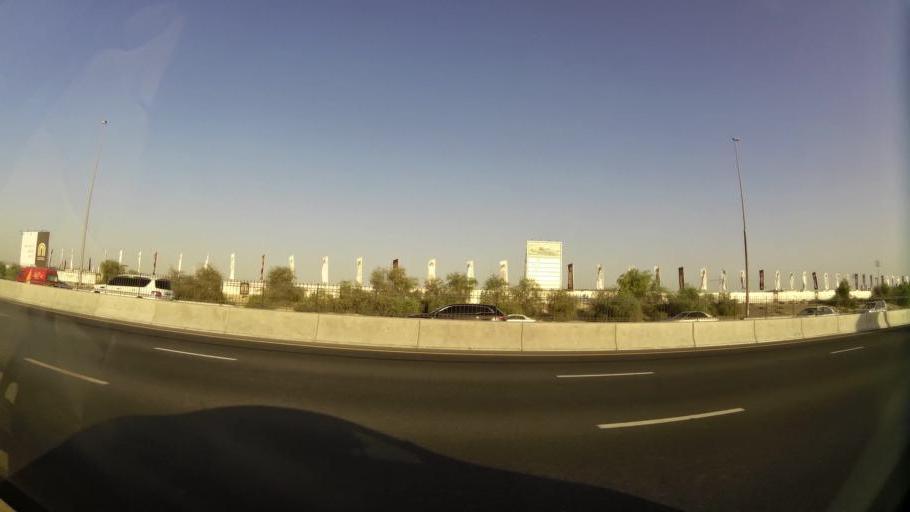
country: AE
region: Ash Shariqah
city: Sharjah
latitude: 25.3187
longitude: 55.4532
